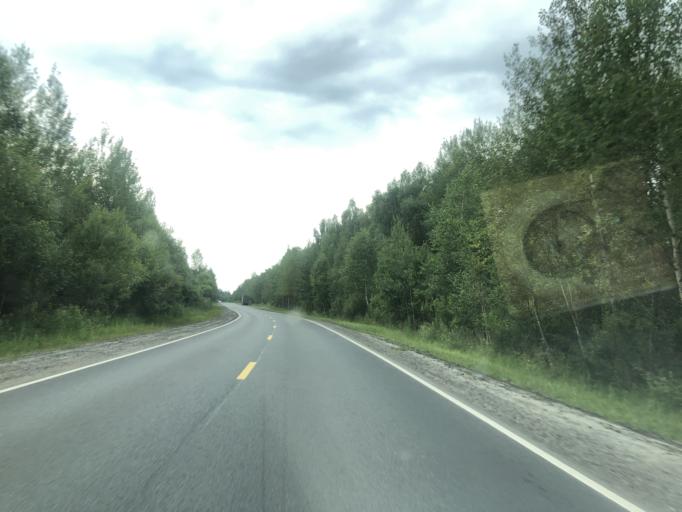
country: RU
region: Ivanovo
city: Verkhniy Landekh
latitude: 56.7658
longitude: 42.4659
